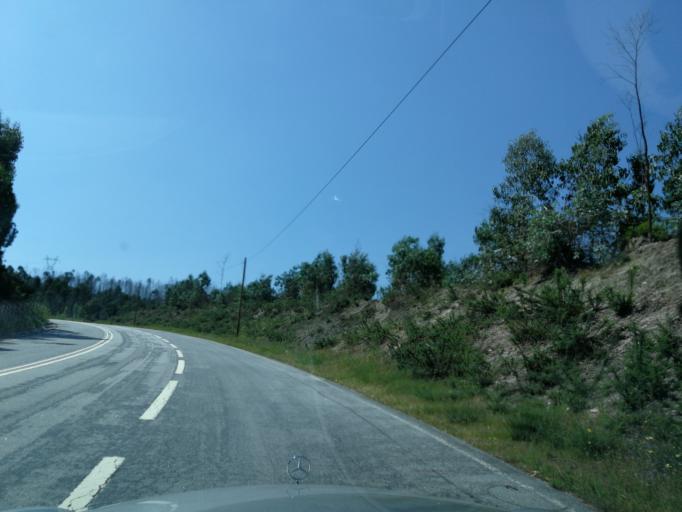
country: PT
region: Braga
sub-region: Braga
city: Adaufe
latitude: 41.5619
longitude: -8.3579
